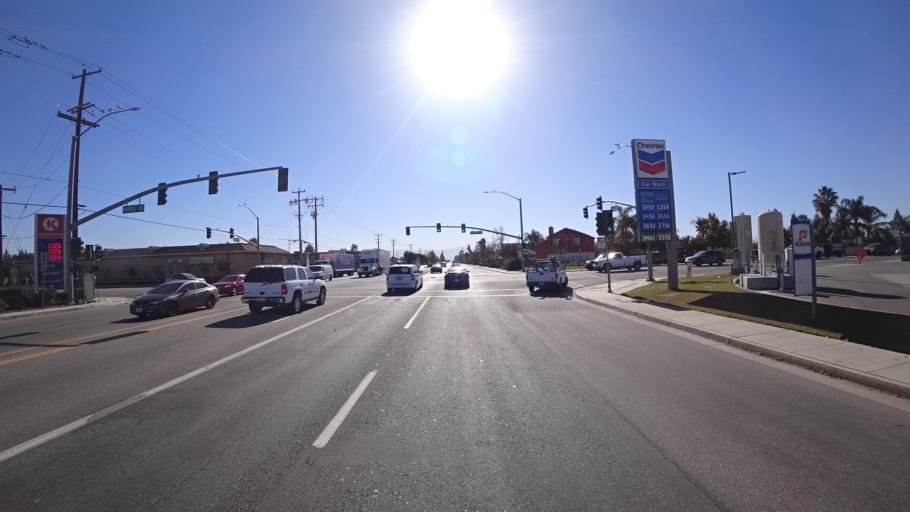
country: US
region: California
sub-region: Kern County
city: Greenfield
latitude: 35.3035
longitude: -119.0568
